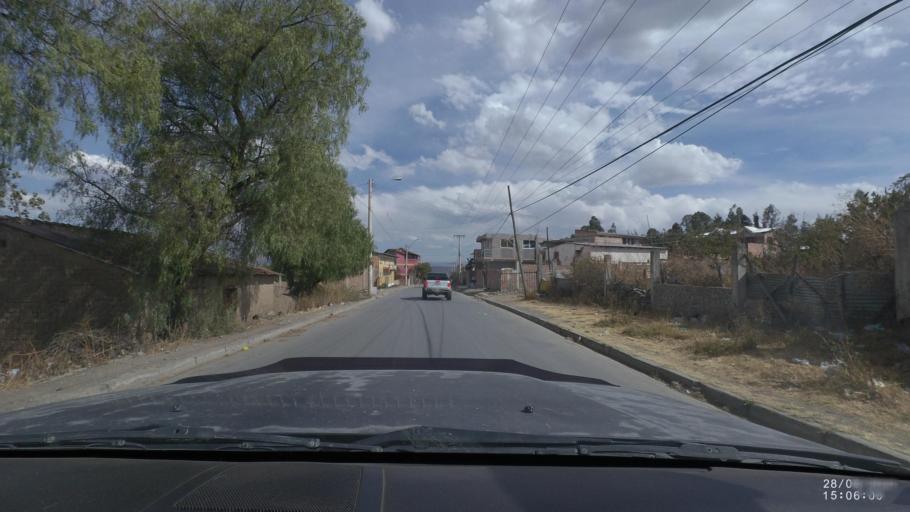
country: BO
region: Cochabamba
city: Cochabamba
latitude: -17.3356
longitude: -66.2840
